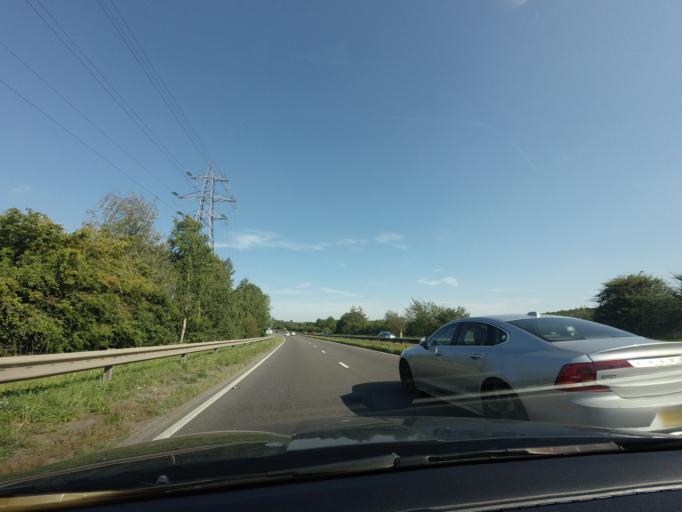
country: GB
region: England
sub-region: Derbyshire
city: Pilsley
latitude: 53.2016
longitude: -1.3622
